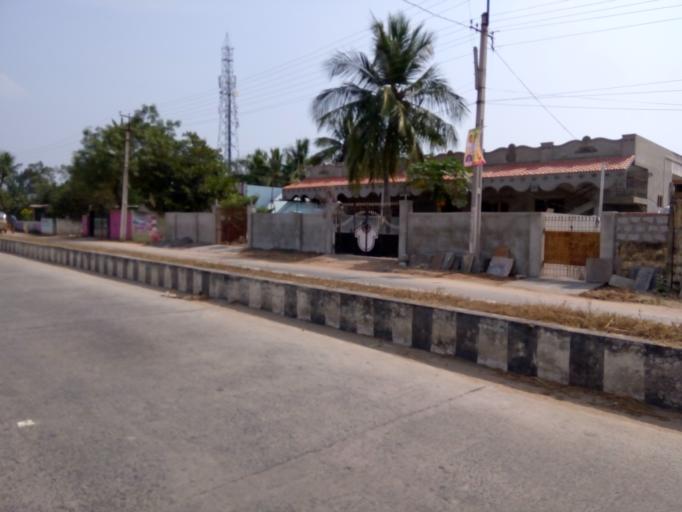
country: IN
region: Andhra Pradesh
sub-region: Prakasam
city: Chirala
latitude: 15.8440
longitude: 80.3773
